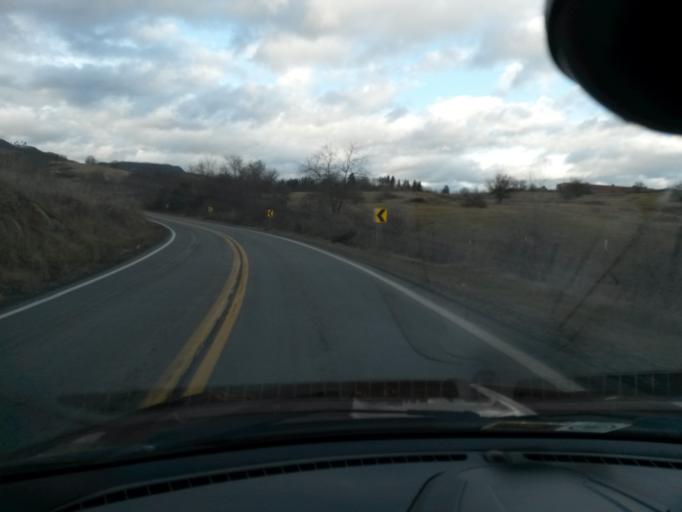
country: US
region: West Virginia
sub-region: Monroe County
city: Union
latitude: 37.5818
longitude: -80.5490
